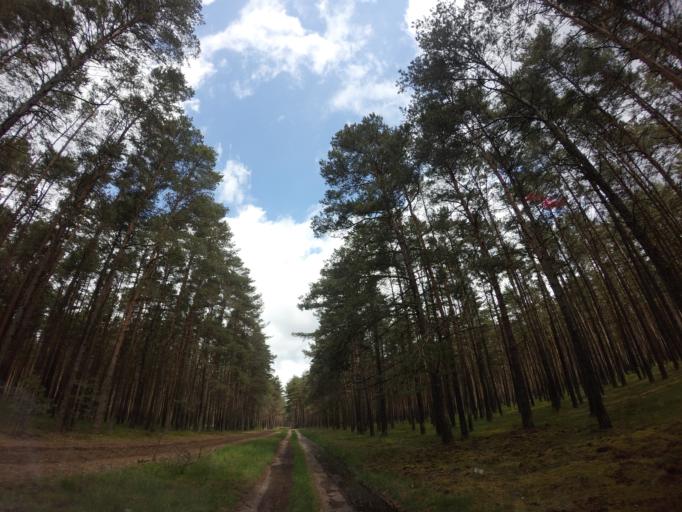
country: PL
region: West Pomeranian Voivodeship
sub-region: Powiat drawski
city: Kalisz Pomorski
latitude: 53.1790
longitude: 15.9009
